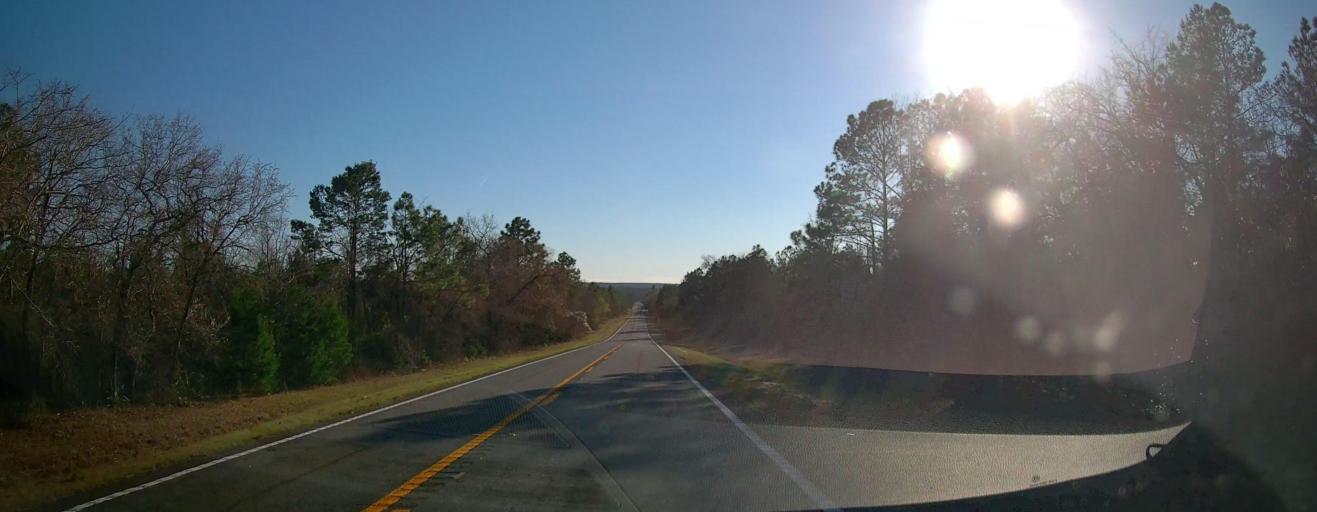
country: US
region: Georgia
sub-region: Taylor County
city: Butler
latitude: 32.5375
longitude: -84.2932
